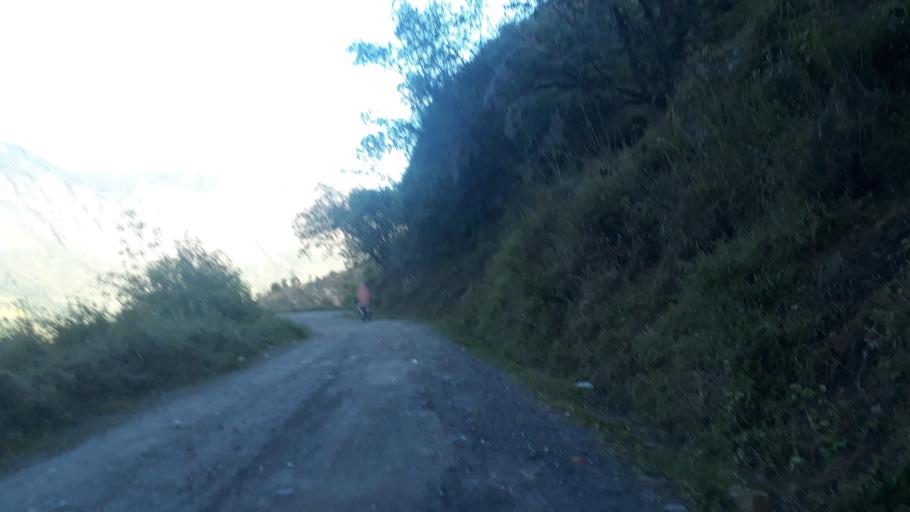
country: CO
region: Boyaca
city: San Mateo
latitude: 6.4010
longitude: -72.5597
